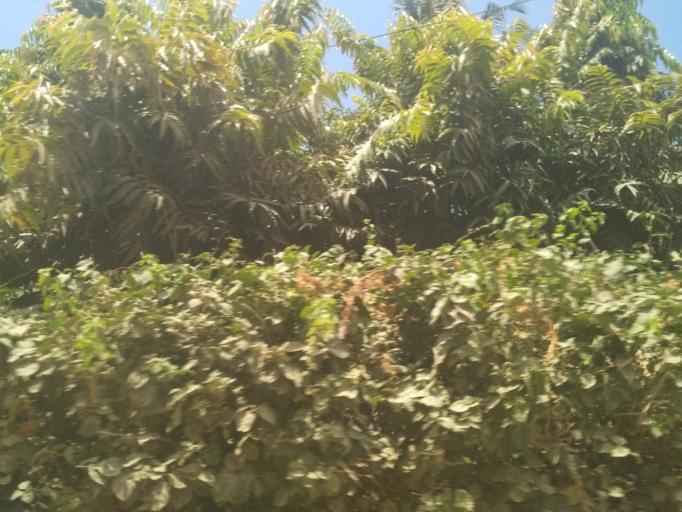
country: TZ
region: Dar es Salaam
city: Magomeni
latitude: -6.7478
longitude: 39.2775
